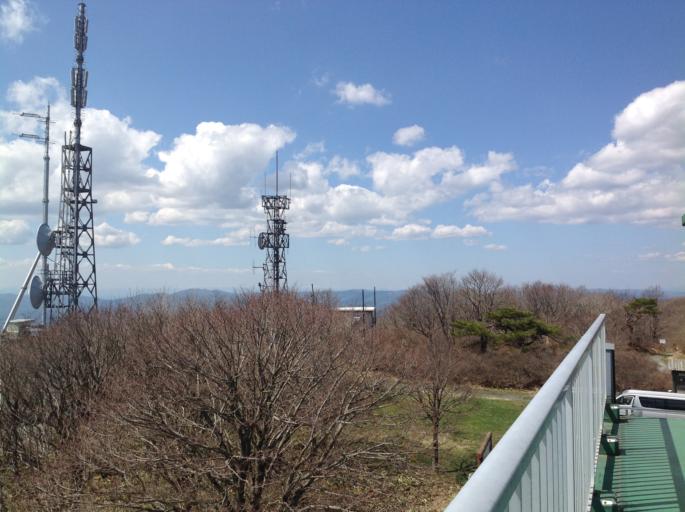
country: JP
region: Iwate
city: Ofunato
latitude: 38.9723
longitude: 141.4451
